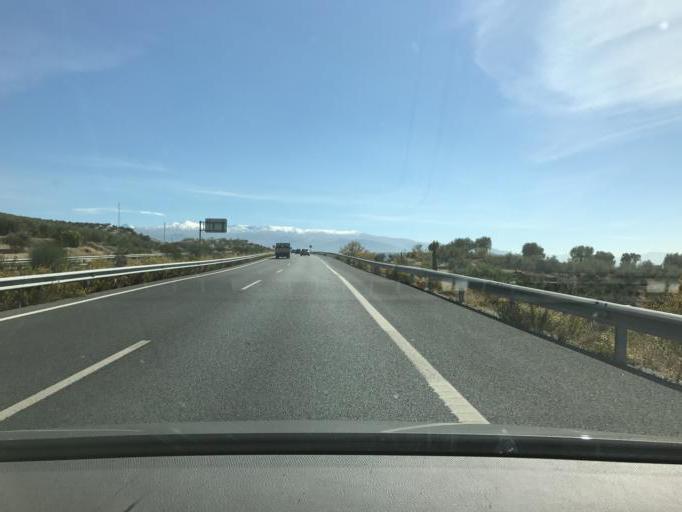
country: ES
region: Andalusia
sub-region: Provincia de Granada
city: Pulianas
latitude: 37.2345
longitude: -3.6005
